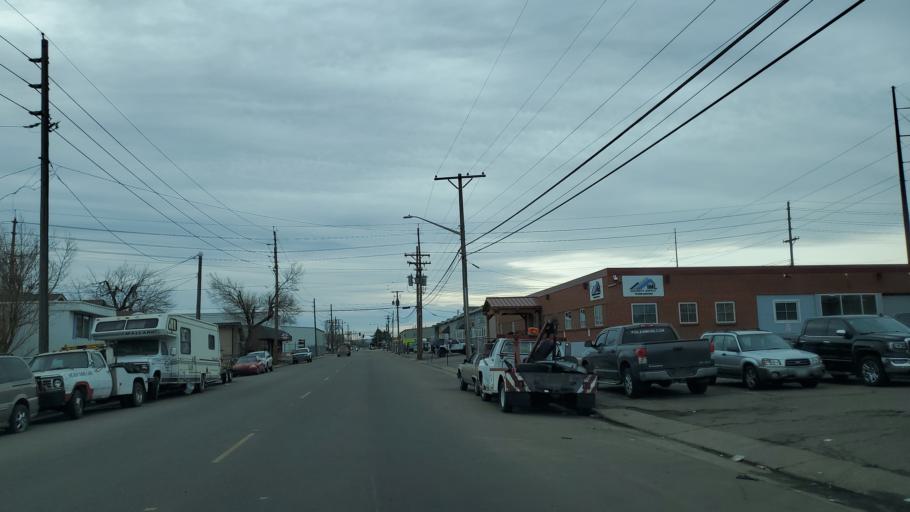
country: US
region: Colorado
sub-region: Denver County
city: Denver
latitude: 39.6993
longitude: -104.9992
